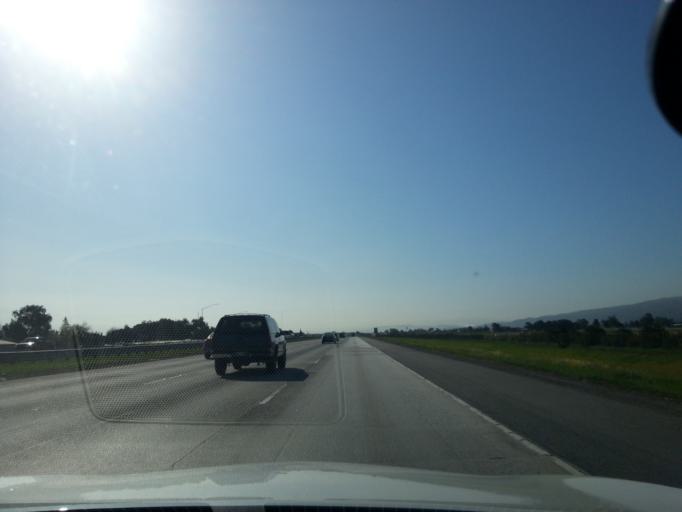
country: US
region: California
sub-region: Santa Clara County
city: San Martin
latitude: 37.0835
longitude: -121.5967
